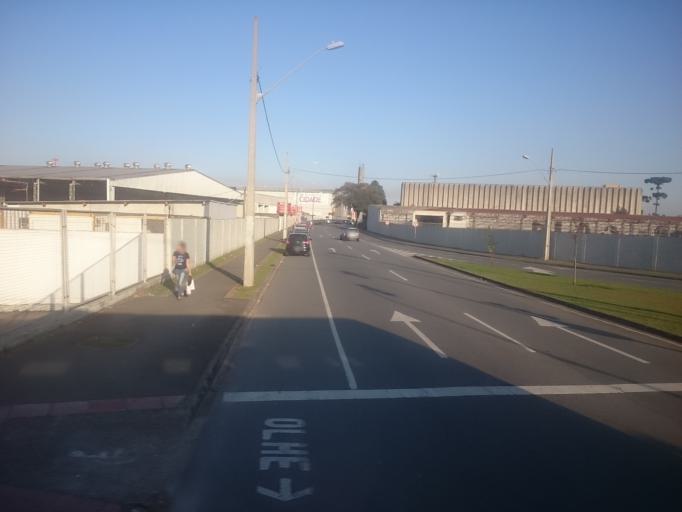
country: BR
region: Parana
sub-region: Curitiba
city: Curitiba
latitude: -25.4704
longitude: -49.2545
